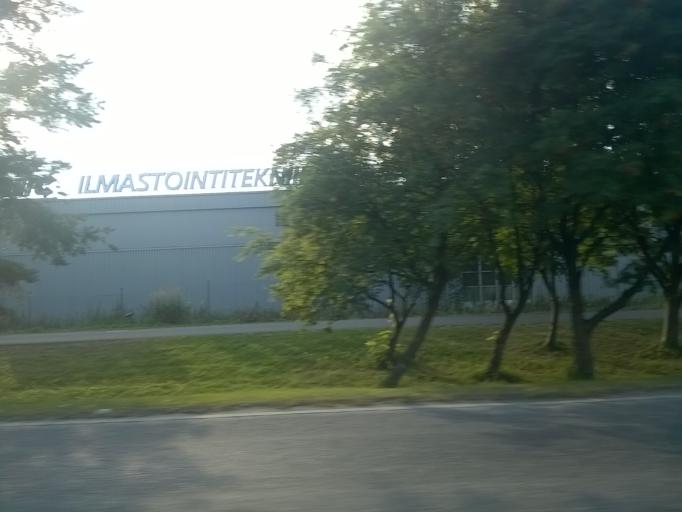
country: FI
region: Pirkanmaa
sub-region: Tampere
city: Tampere
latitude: 61.4705
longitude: 23.7635
